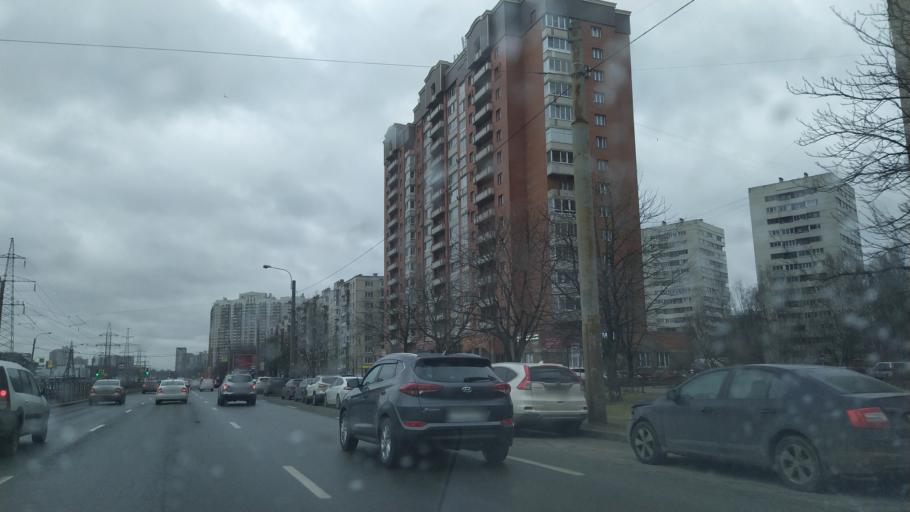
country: RU
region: St.-Petersburg
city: Komendantsky aerodrom
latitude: 60.0043
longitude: 30.2876
